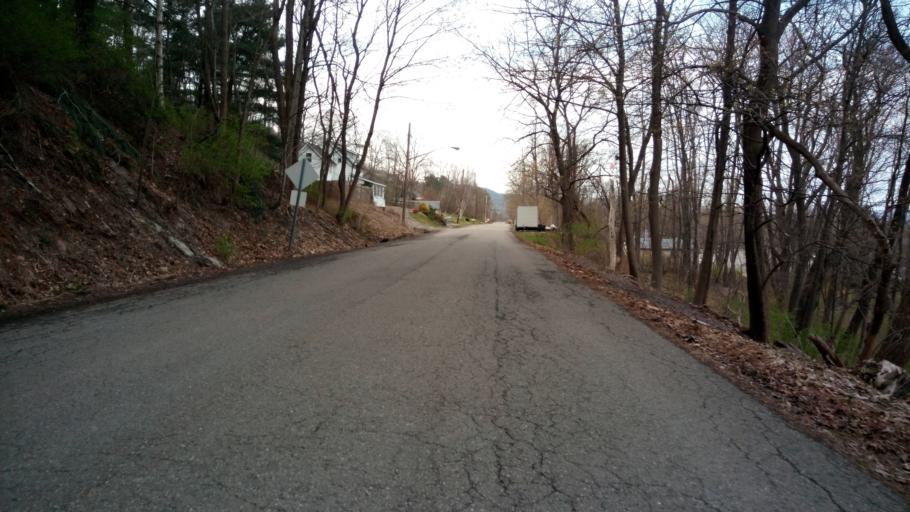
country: US
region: New York
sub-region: Chemung County
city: Southport
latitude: 42.0642
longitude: -76.8207
